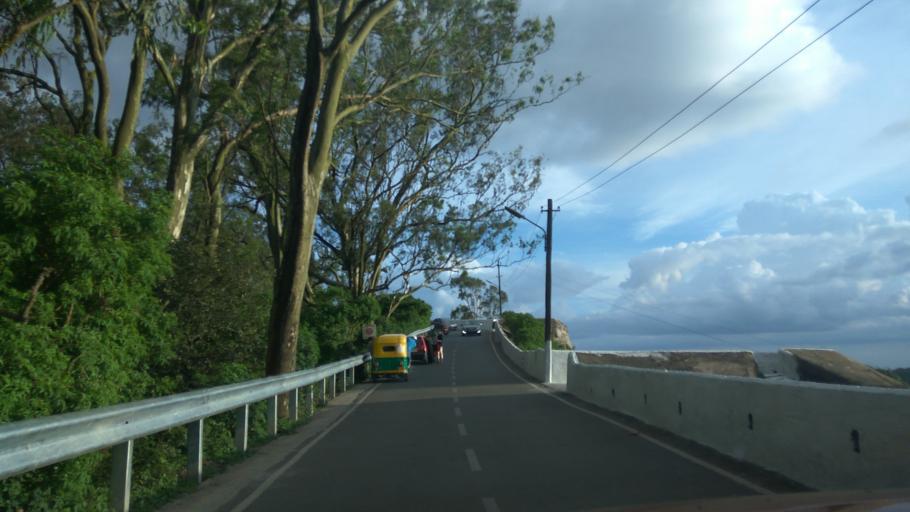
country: IN
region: Karnataka
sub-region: Chikkaballapur
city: Chik Ballapur
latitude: 13.3705
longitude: 77.6803
